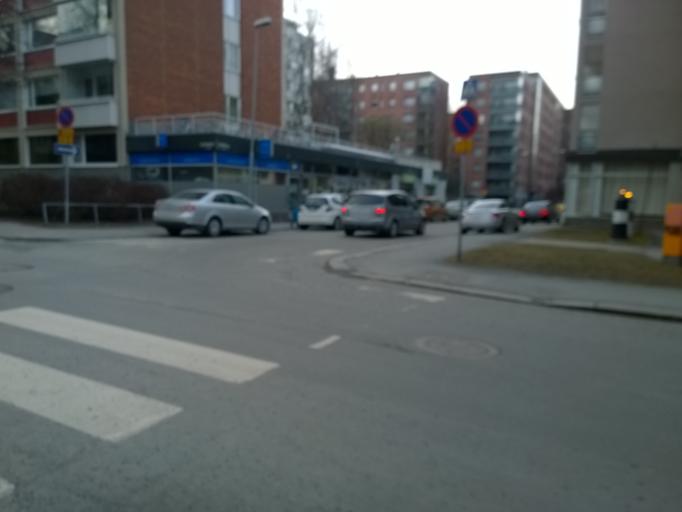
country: FI
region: Pirkanmaa
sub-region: Tampere
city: Tampere
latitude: 61.4924
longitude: 23.7513
